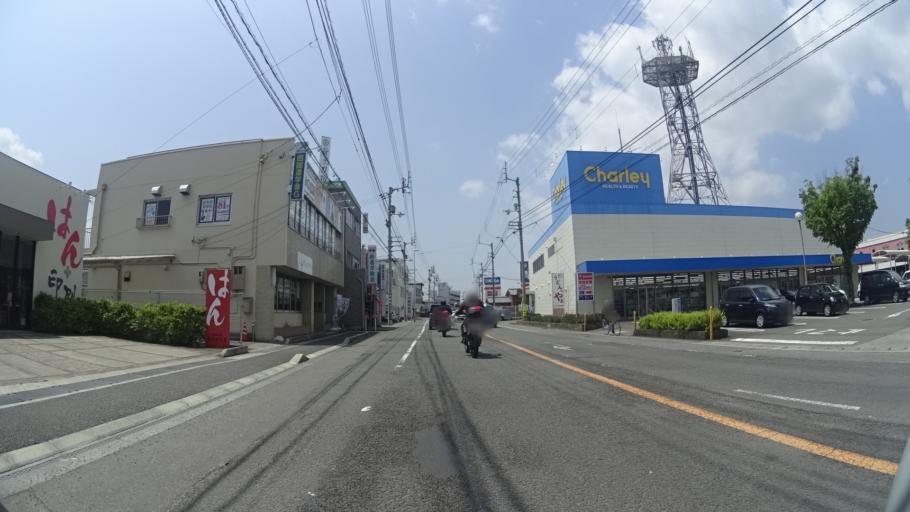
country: JP
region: Tokushima
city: Kamojimacho-jogejima
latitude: 34.0685
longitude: 134.3596
